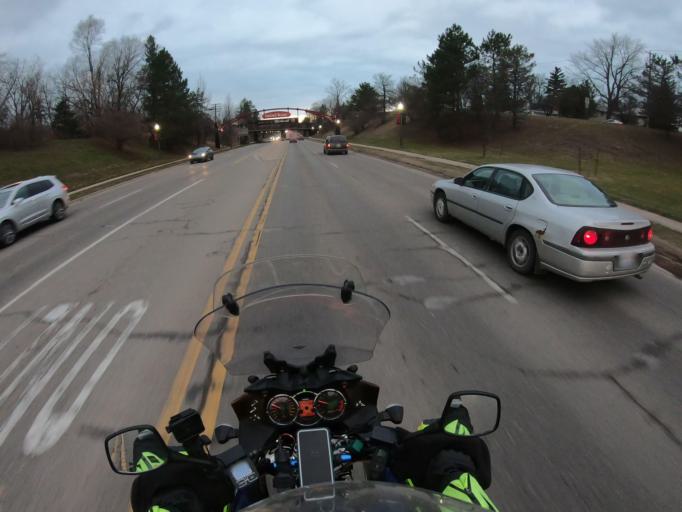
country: US
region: Michigan
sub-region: Genesee County
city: Grand Blanc
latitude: 42.9316
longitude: -83.6346
